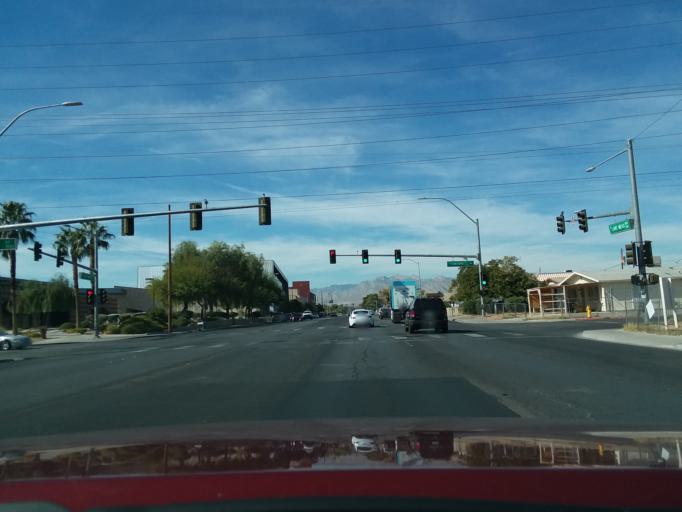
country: US
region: Nevada
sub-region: Clark County
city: Las Vegas
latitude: 36.1958
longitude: -115.1558
